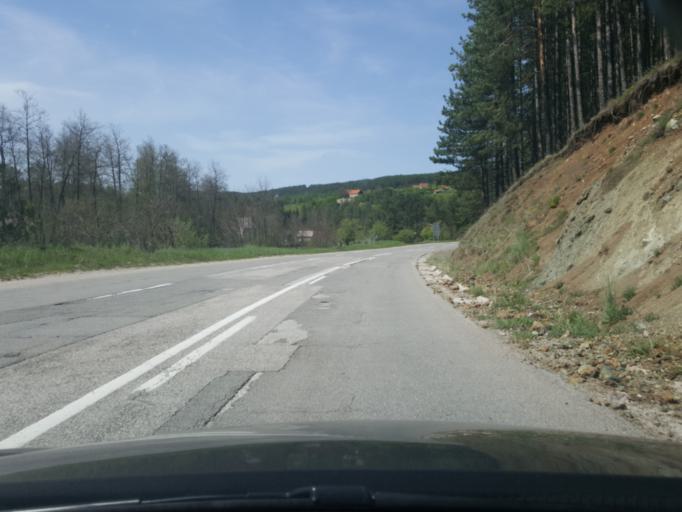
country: RS
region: Central Serbia
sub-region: Zlatiborski Okrug
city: Bajina Basta
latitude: 43.8383
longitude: 19.6056
